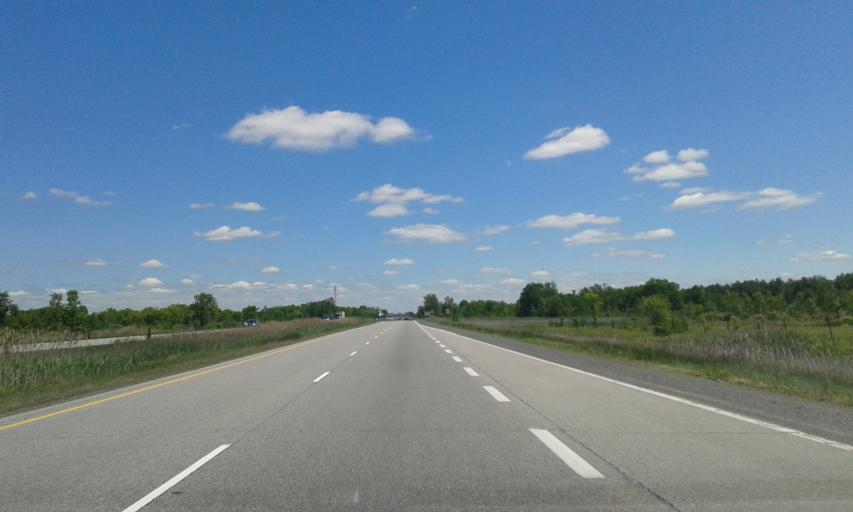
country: US
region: New York
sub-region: St. Lawrence County
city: Norfolk
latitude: 44.9554
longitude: -75.1040
